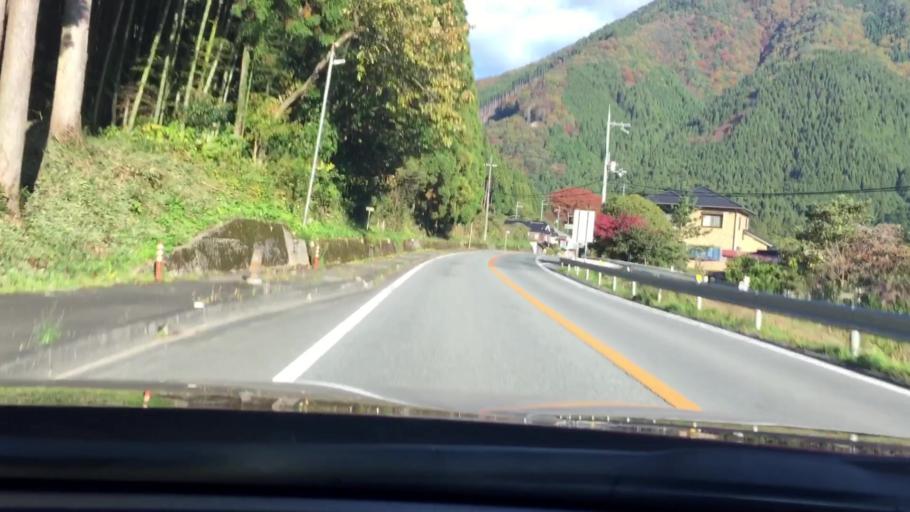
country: JP
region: Hyogo
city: Yamazakicho-nakabirose
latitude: 35.1356
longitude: 134.5575
